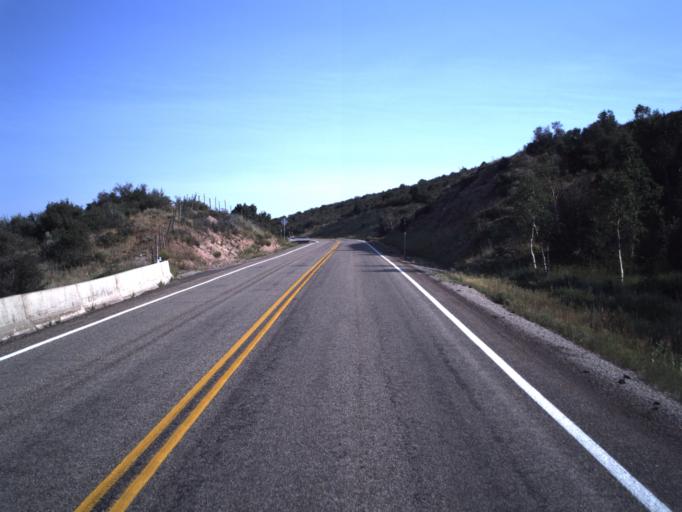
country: US
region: Utah
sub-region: Uintah County
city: Vernal
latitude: 40.6655
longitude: -109.4812
